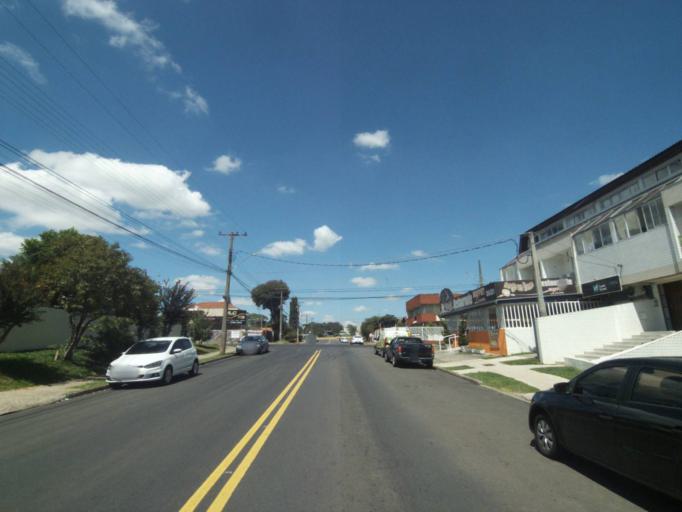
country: BR
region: Parana
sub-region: Pinhais
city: Pinhais
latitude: -25.4382
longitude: -49.2217
